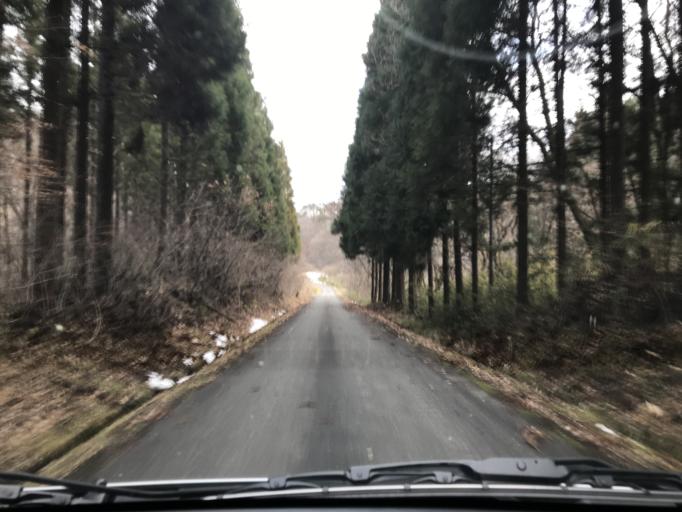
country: JP
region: Iwate
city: Ichinoseki
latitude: 38.9734
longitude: 141.0497
